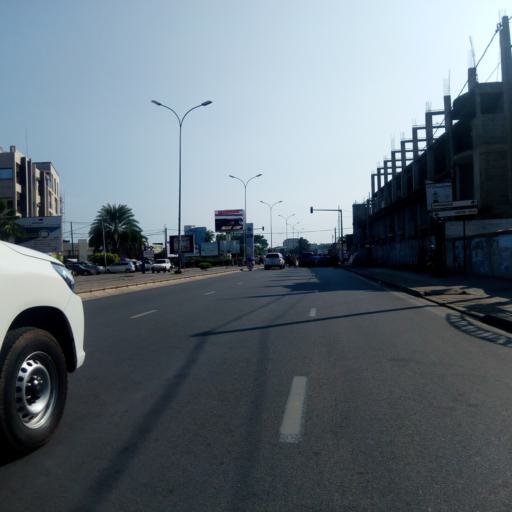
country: TG
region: Maritime
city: Lome
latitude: 6.1363
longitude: 1.2200
